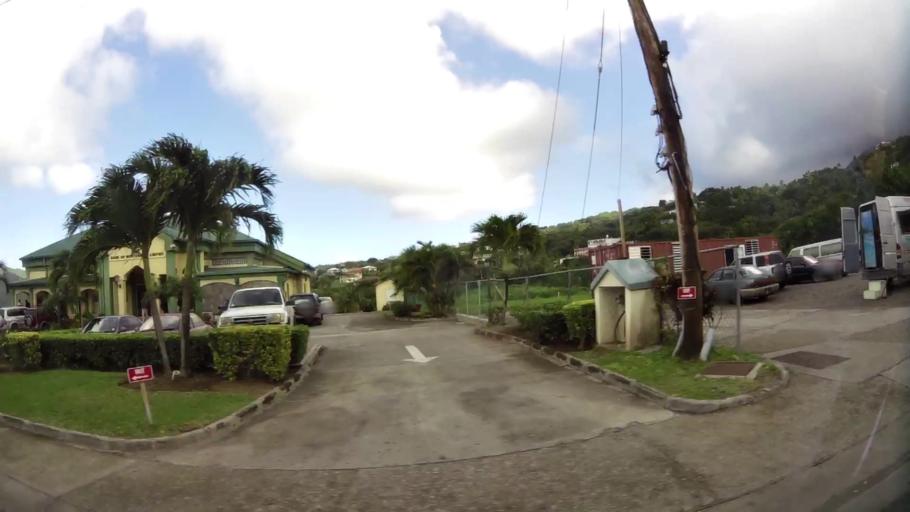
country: MS
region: Saint Peter
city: Brades
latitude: 16.7831
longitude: -62.2071
